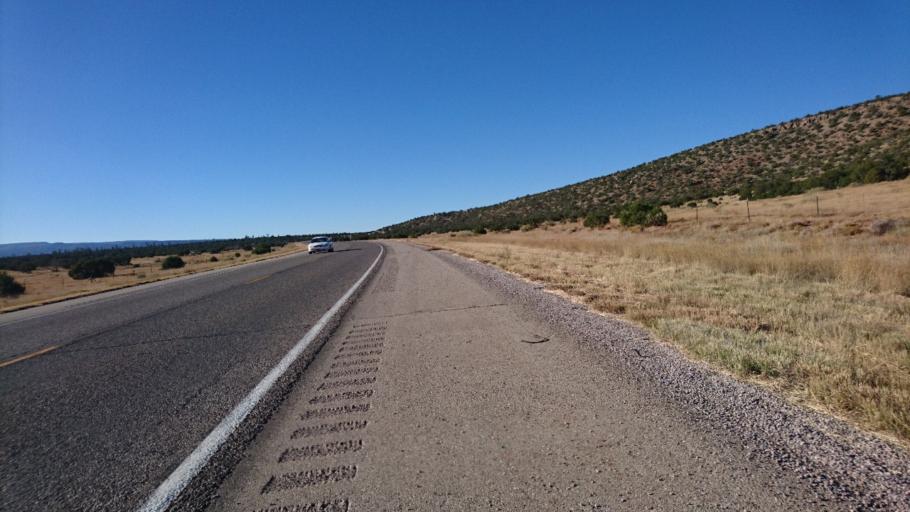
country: US
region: New Mexico
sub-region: Cibola County
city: Grants
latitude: 34.9741
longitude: -107.9120
